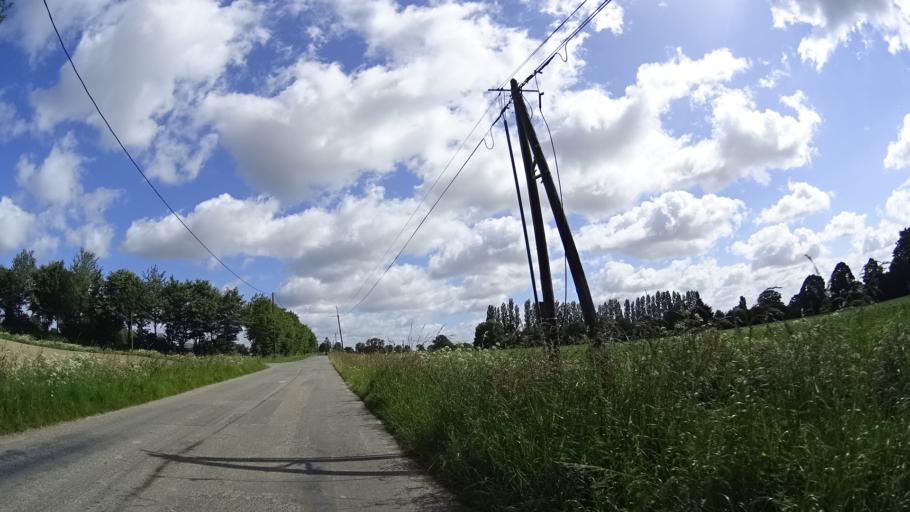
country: FR
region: Brittany
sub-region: Departement d'Ille-et-Vilaine
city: La Meziere
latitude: 48.2304
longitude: -1.7413
